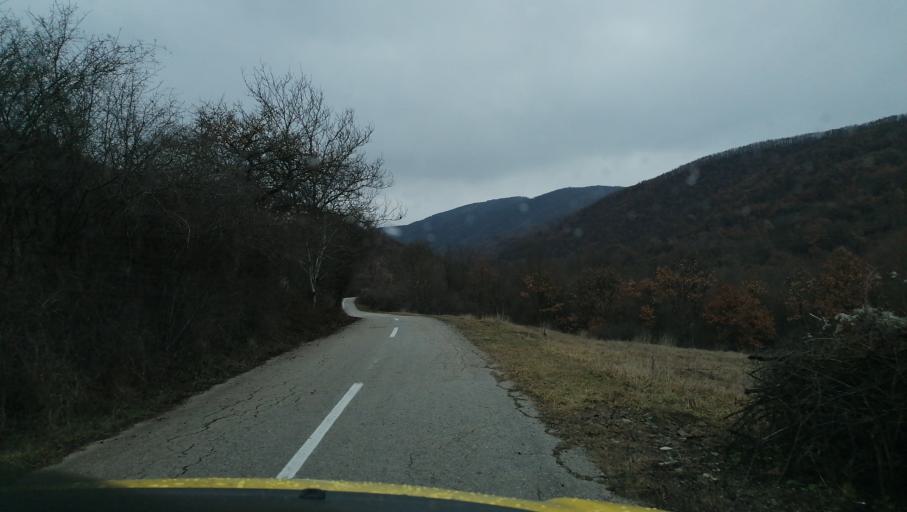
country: RS
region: Central Serbia
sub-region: Pirotski Okrug
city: Dimitrovgrad
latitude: 42.9591
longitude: 22.7826
